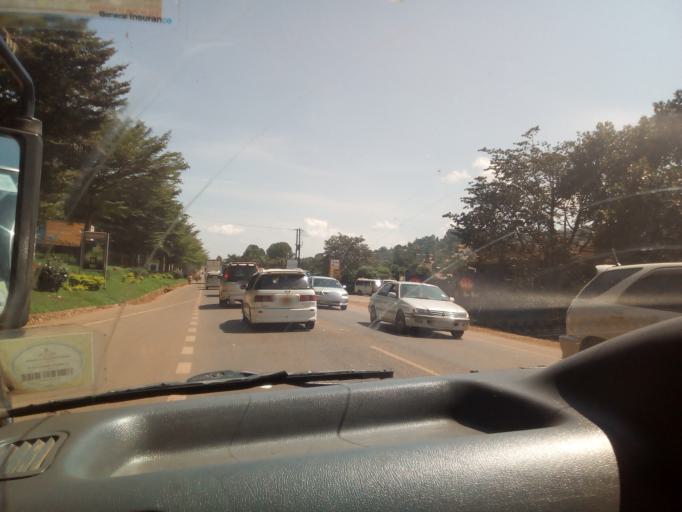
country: UG
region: Central Region
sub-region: Wakiso District
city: Kajansi
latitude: 0.2428
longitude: 32.5568
